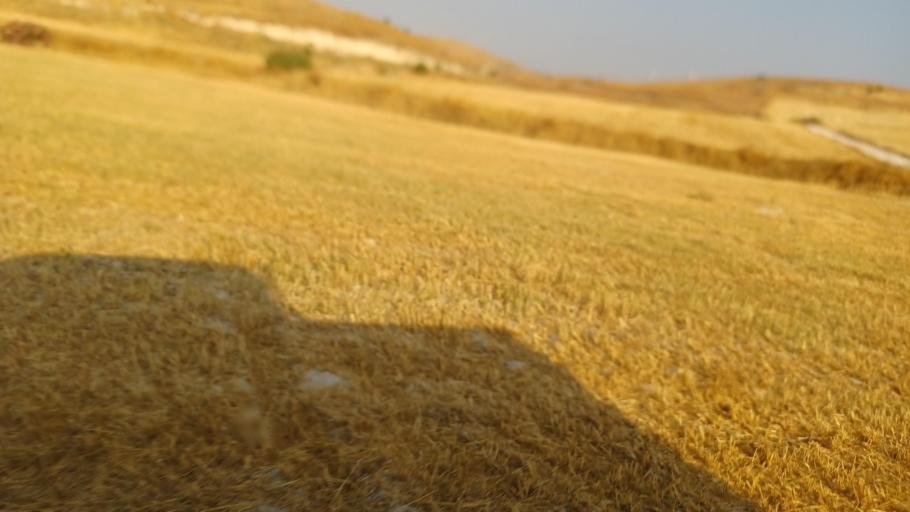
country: CY
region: Larnaka
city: Psevdas
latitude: 34.9170
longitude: 33.5048
